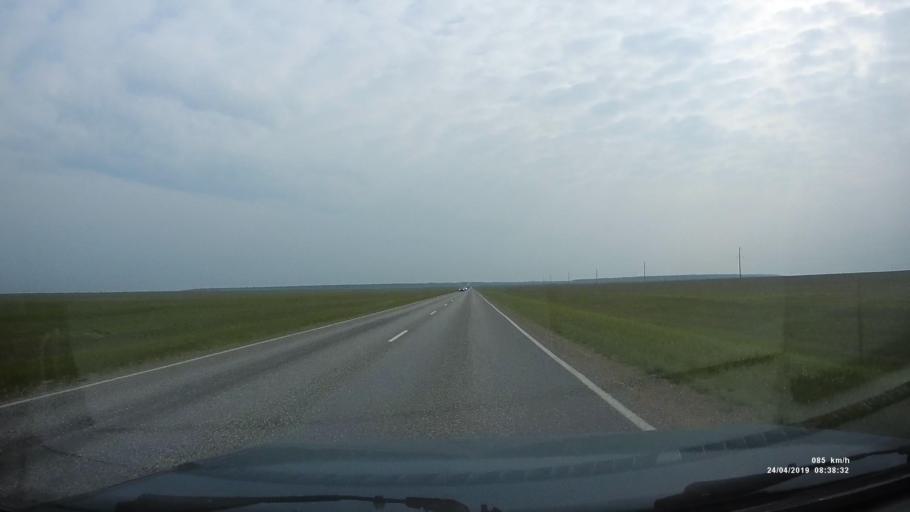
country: RU
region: Kalmykiya
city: Arshan'
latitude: 46.2159
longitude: 43.9690
